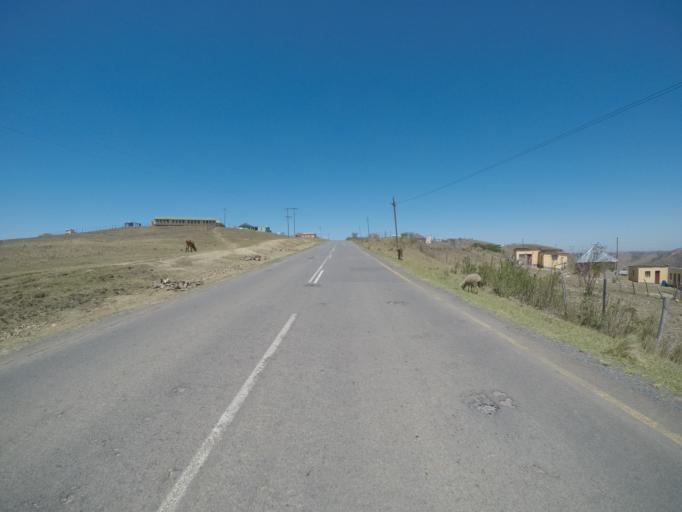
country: ZA
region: Eastern Cape
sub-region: OR Tambo District Municipality
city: Mthatha
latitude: -31.9039
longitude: 28.9472
